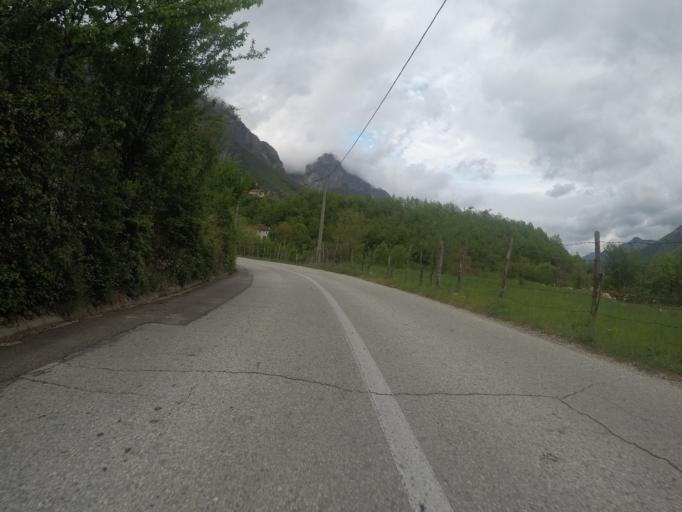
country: BA
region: Federation of Bosnia and Herzegovina
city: Siroki Brijeg
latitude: 43.5434
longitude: 17.5534
